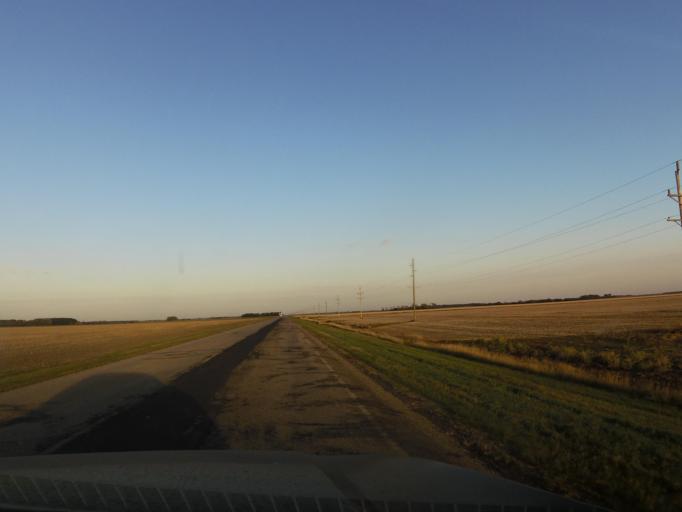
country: CA
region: Manitoba
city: Altona
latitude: 48.9634
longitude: -97.6179
